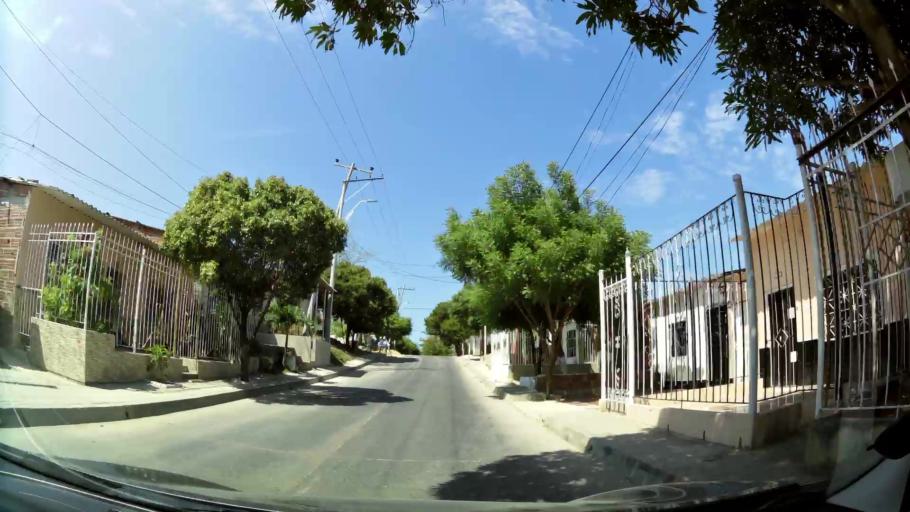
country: CO
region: Atlantico
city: Barranquilla
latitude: 10.9658
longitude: -74.8288
